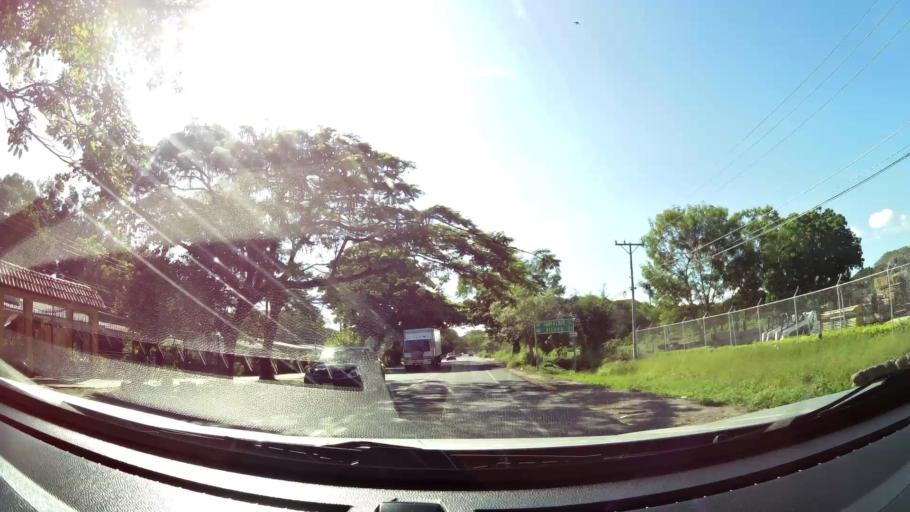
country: CR
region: Guanacaste
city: Liberia
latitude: 10.6253
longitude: -85.4473
